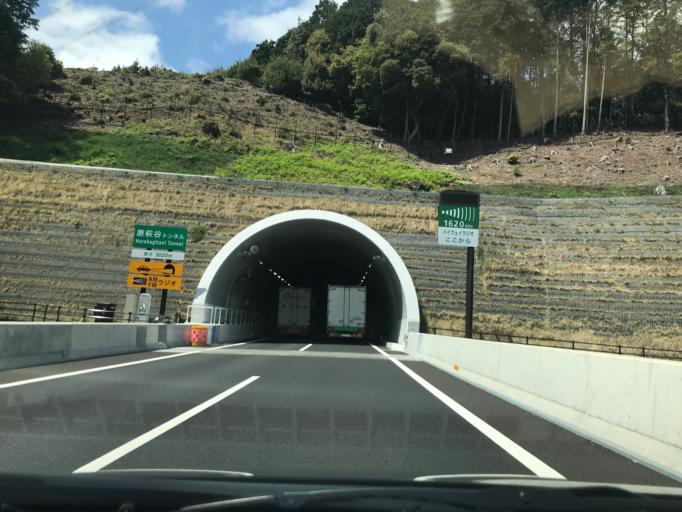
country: JP
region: Osaka
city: Takatsuki
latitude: 34.9021
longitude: 135.6012
